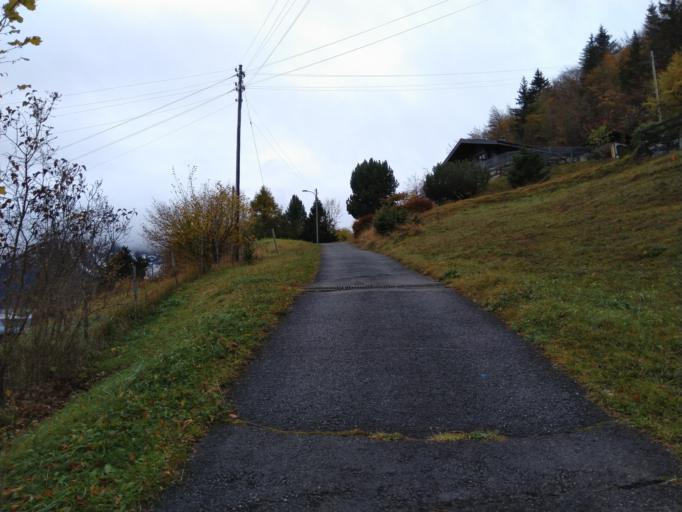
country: CH
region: Valais
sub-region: Monthey District
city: Vouvry
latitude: 46.3206
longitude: 6.8747
